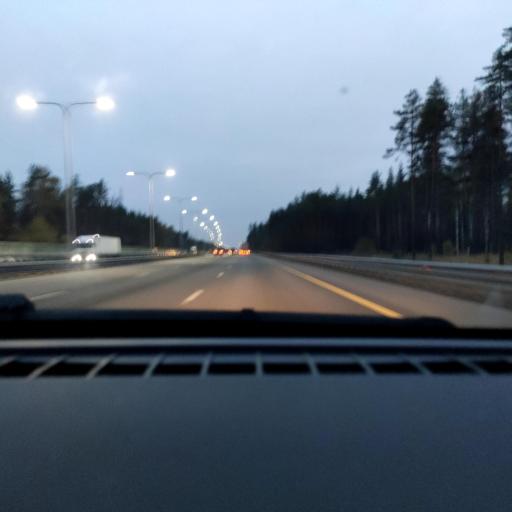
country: RU
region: Voronezj
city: Somovo
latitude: 51.7149
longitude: 39.3080
